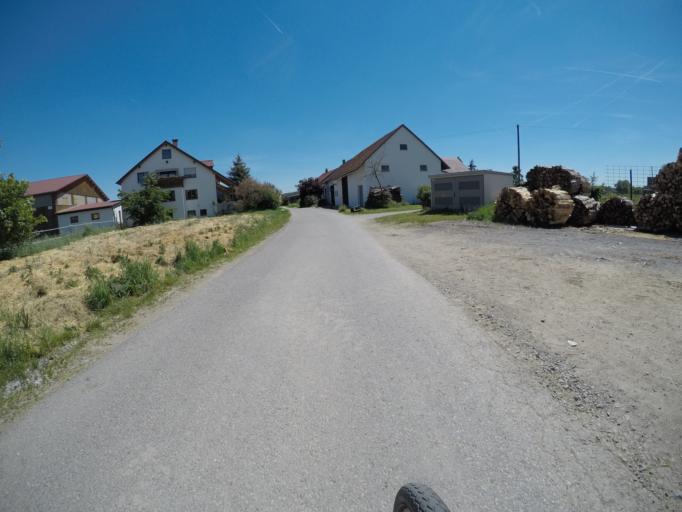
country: DE
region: Baden-Wuerttemberg
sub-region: Regierungsbezirk Stuttgart
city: Renningen
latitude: 48.7639
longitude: 8.9423
